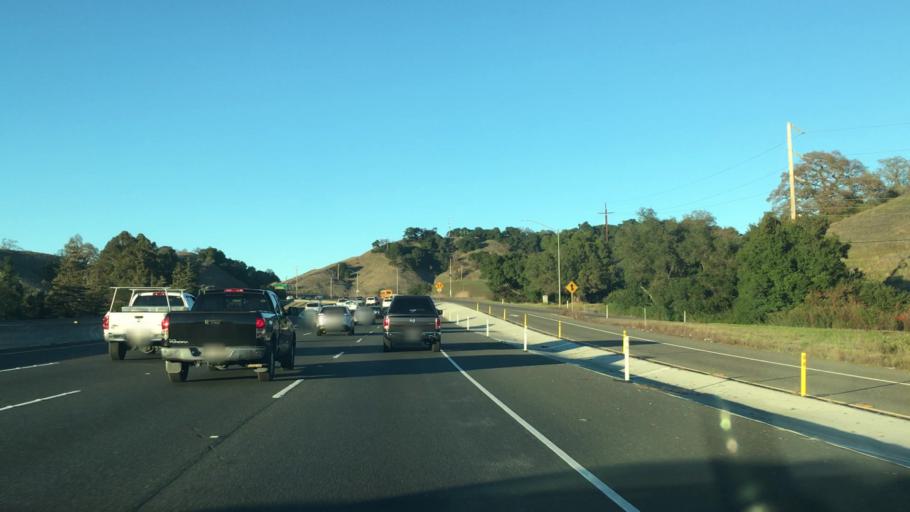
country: US
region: California
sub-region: Marin County
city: Santa Venetia
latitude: 38.0339
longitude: -122.5364
